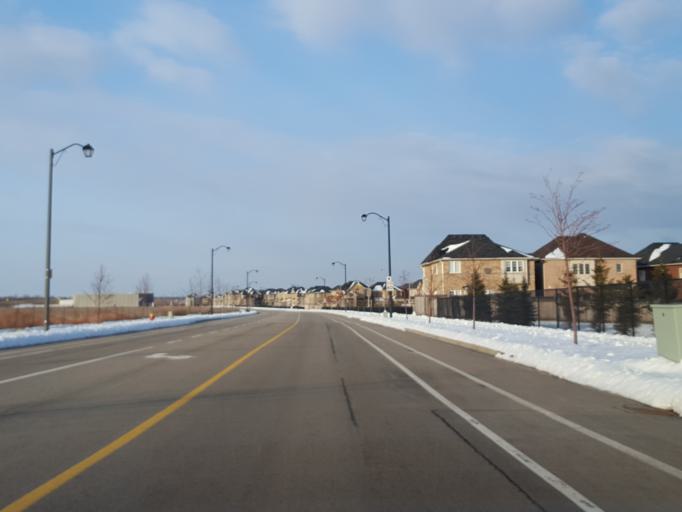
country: CA
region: Ontario
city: Burlington
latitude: 43.4003
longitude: -79.8292
